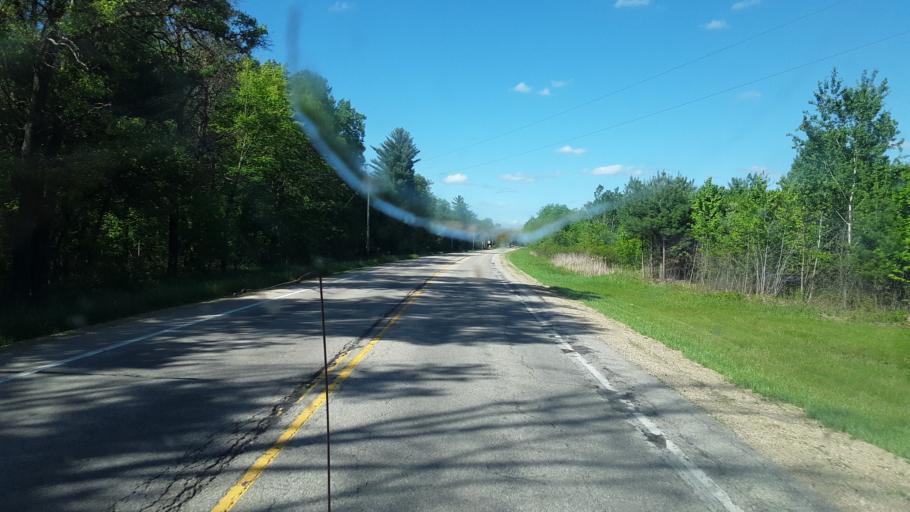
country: US
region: Wisconsin
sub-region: Juneau County
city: New Lisbon
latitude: 43.9092
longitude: -90.1278
